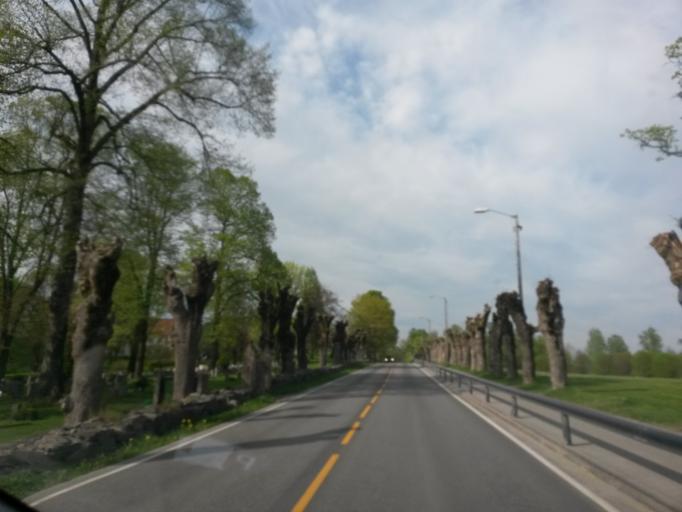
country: NO
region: Akershus
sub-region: Asker
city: Asker
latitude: 59.8435
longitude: 10.4381
